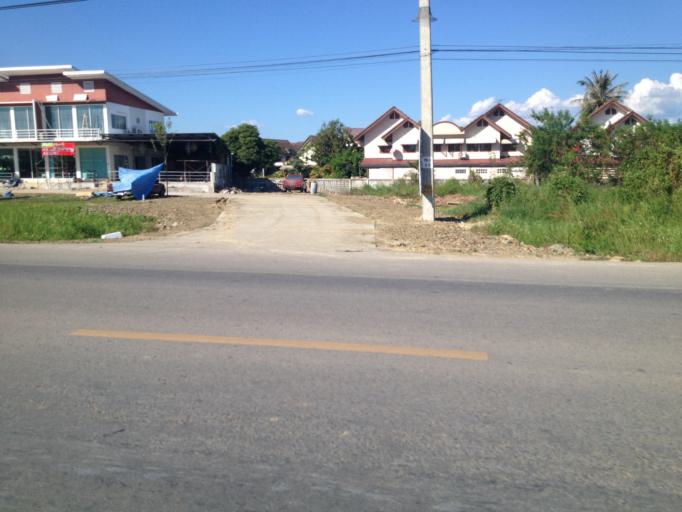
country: TH
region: Chiang Mai
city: Hang Dong
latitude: 18.7201
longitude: 98.9652
